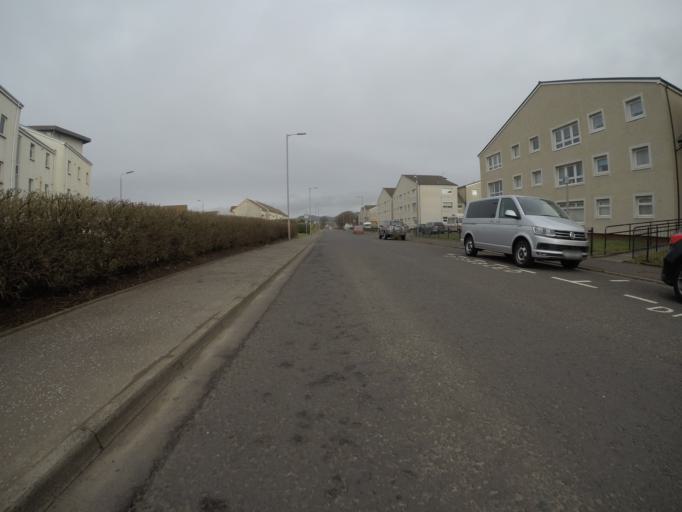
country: GB
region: Scotland
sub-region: North Ayrshire
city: Ardrossan
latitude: 55.6415
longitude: -4.8158
